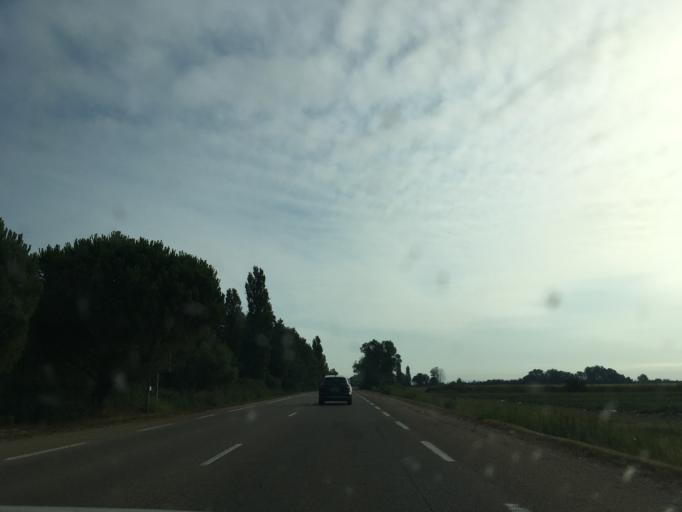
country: FR
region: Languedoc-Roussillon
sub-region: Departement du Gard
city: Saint-Gilles
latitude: 43.5876
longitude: 4.4607
